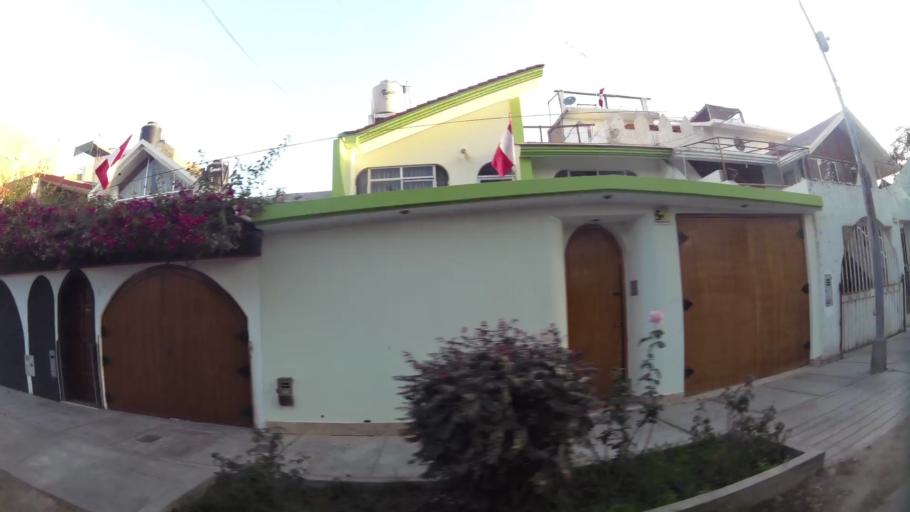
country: PE
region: Ica
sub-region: Provincia de Ica
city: Ica
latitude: -14.0868
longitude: -75.7250
